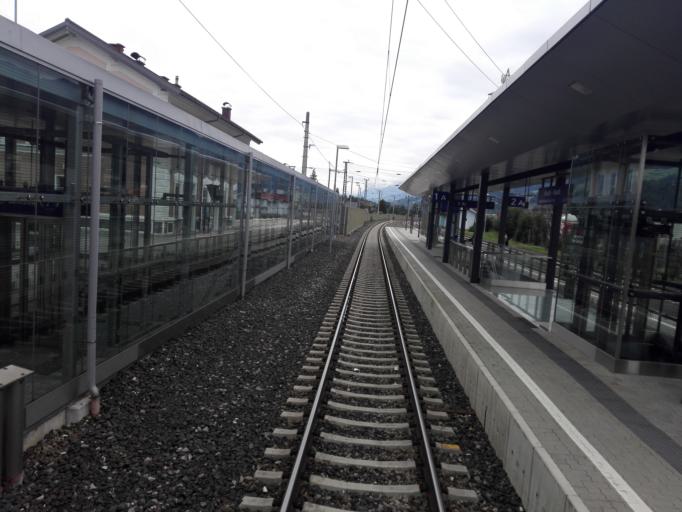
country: AT
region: Salzburg
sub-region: Politischer Bezirk Zell am See
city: Bruck an der Grossglocknerstrasse
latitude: 47.2847
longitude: 12.8279
